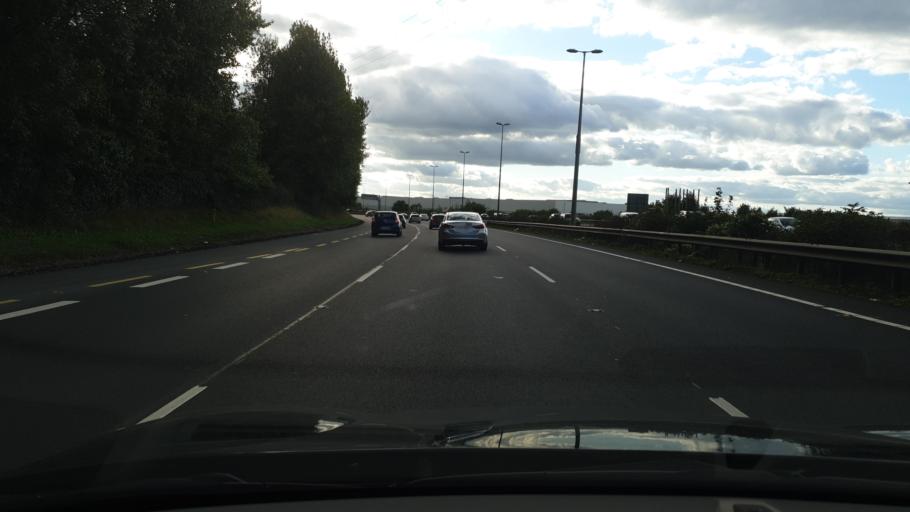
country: IE
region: Leinster
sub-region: South Dublin
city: Saggart
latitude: 53.2907
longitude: -6.4422
